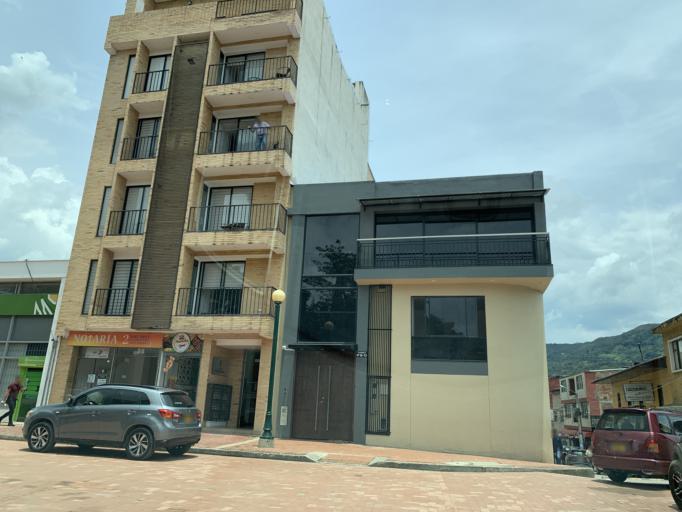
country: CO
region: Boyaca
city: Moniquira
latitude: 5.8777
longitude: -73.5718
